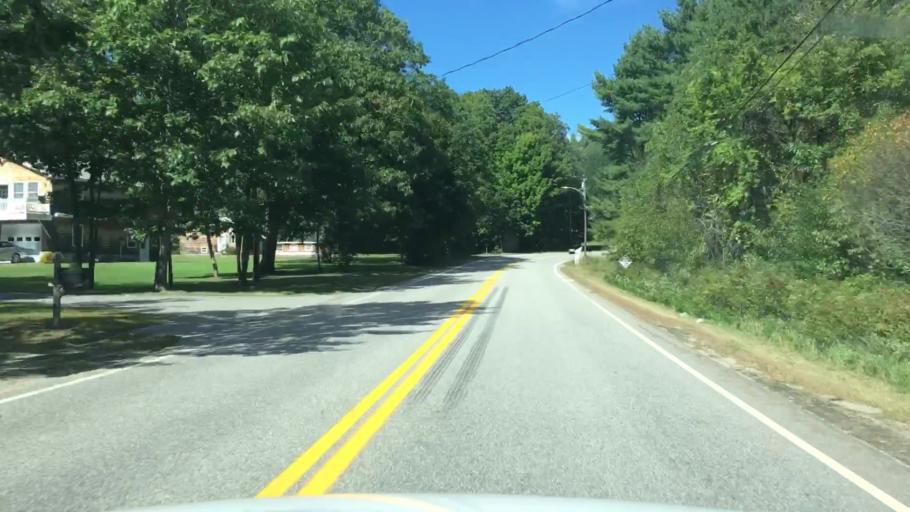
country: US
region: Maine
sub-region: Cumberland County
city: Westbrook
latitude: 43.6287
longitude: -70.4088
